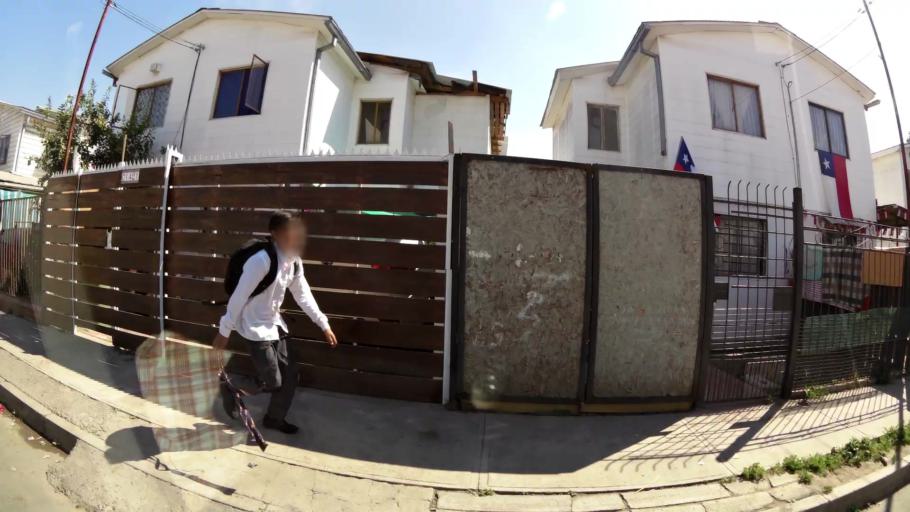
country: CL
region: Santiago Metropolitan
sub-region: Provincia de Cordillera
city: Puente Alto
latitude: -33.6285
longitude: -70.6095
